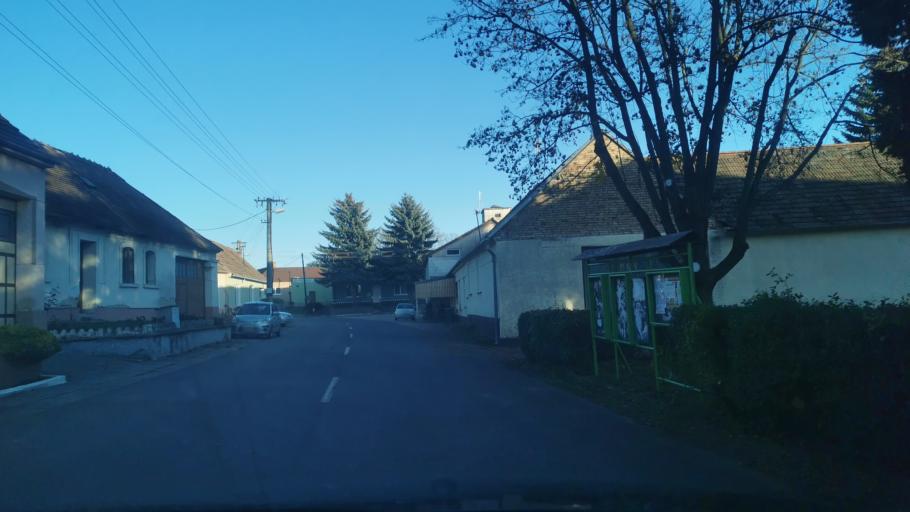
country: CZ
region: South Moravian
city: Sudomerice
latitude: 48.7841
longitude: 17.3024
